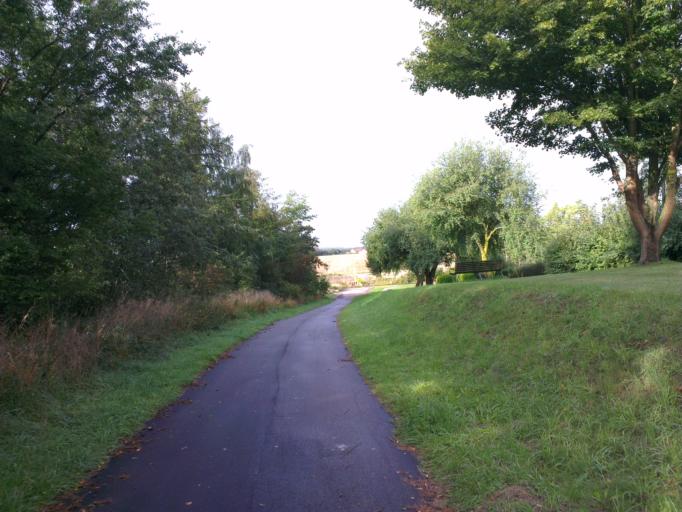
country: DK
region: Capital Region
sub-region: Frederikssund Kommune
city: Frederikssund
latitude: 55.8182
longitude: 12.0888
